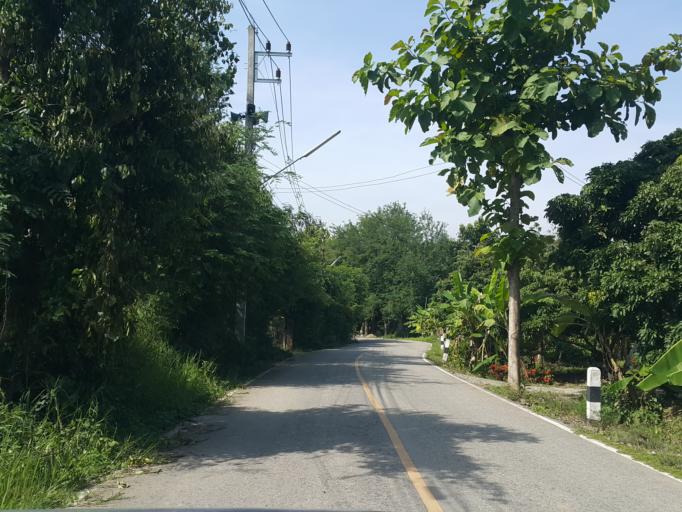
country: TH
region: Chiang Mai
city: Saraphi
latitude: 18.6970
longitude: 99.0770
